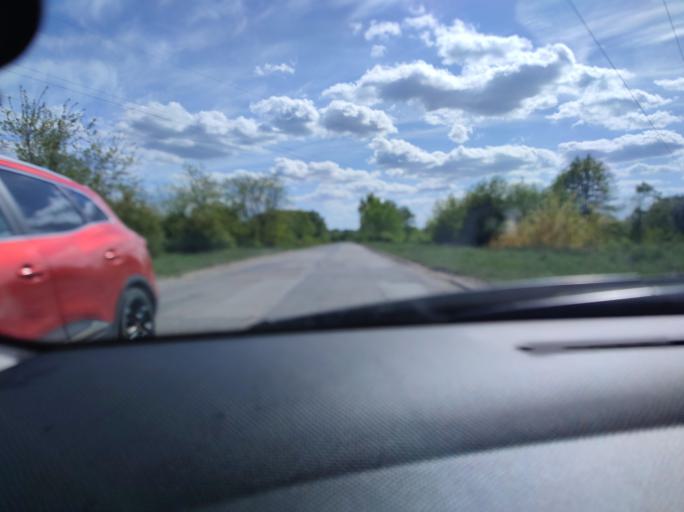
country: PL
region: West Pomeranian Voivodeship
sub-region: Powiat policki
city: Police
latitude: 53.5776
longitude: 14.5299
